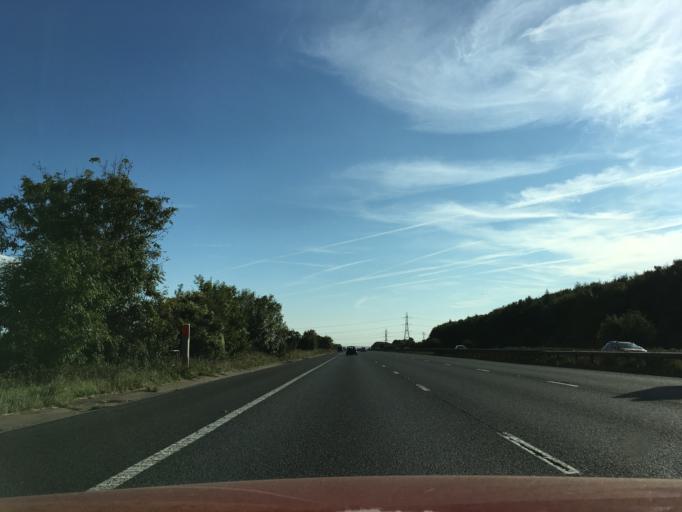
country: GB
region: England
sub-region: South Gloucestershire
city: Tytherington
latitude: 51.5934
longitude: -2.4895
